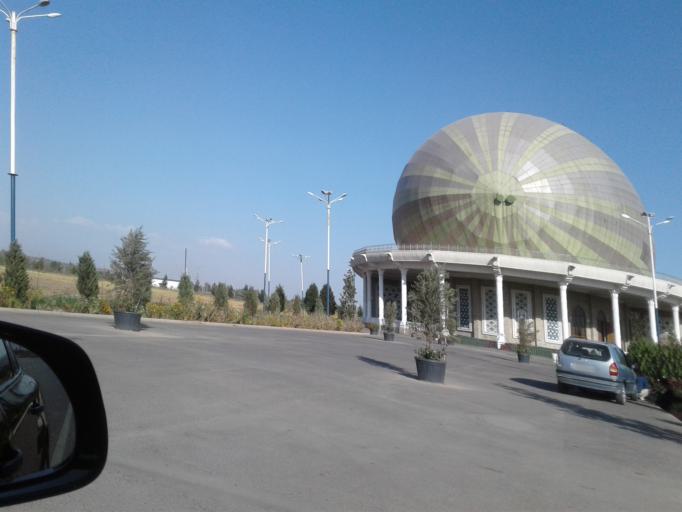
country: TJ
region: Republican Subordination
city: Hisor
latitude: 38.5390
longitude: 68.5590
